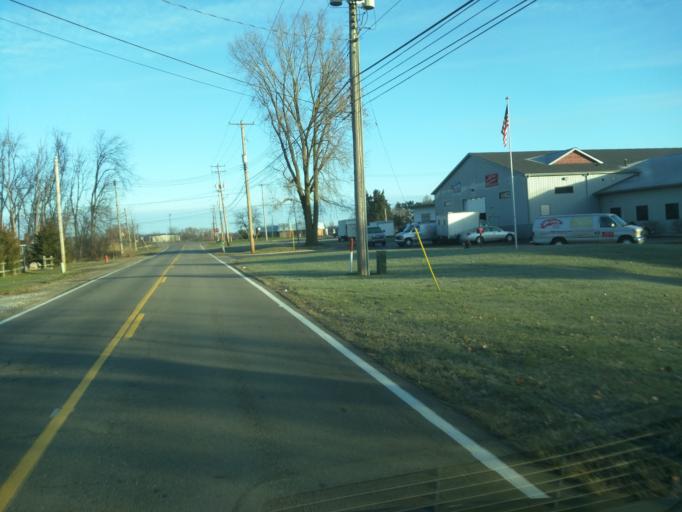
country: US
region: Michigan
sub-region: Ingham County
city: Edgemont Park
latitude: 42.7688
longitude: -84.6028
